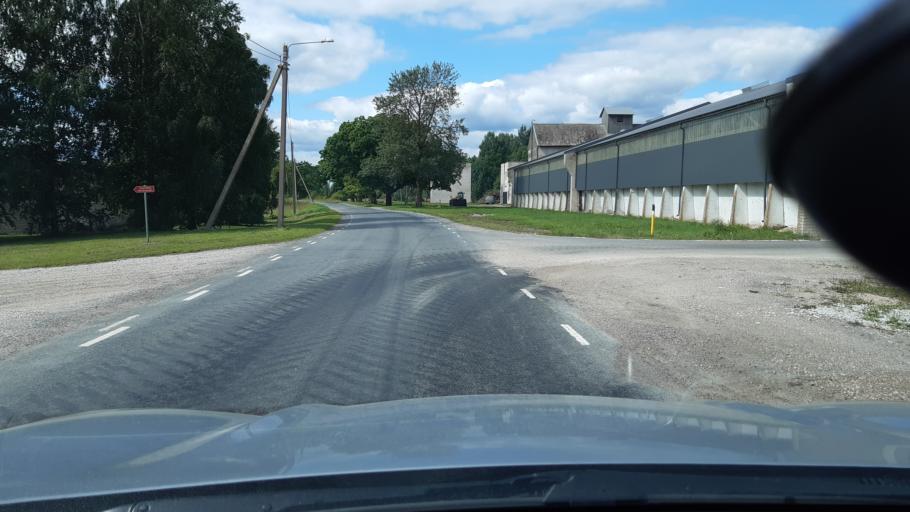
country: EE
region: Raplamaa
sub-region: Jaervakandi vald
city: Jarvakandi
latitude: 58.7976
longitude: 24.9230
